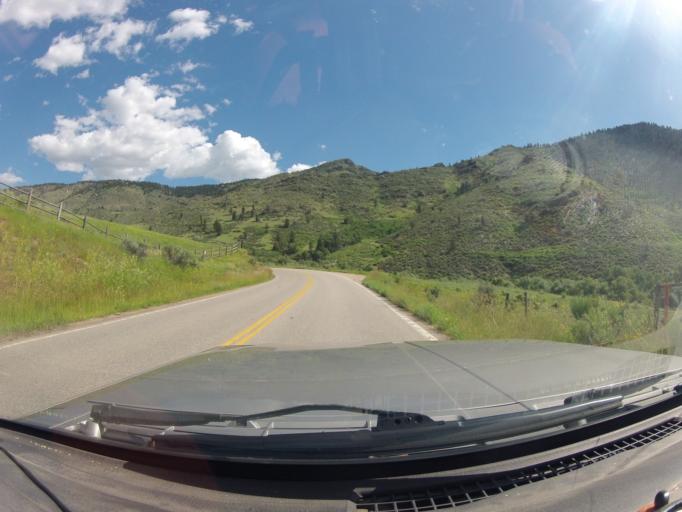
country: US
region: Colorado
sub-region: Larimer County
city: Laporte
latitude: 40.5550
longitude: -105.2909
